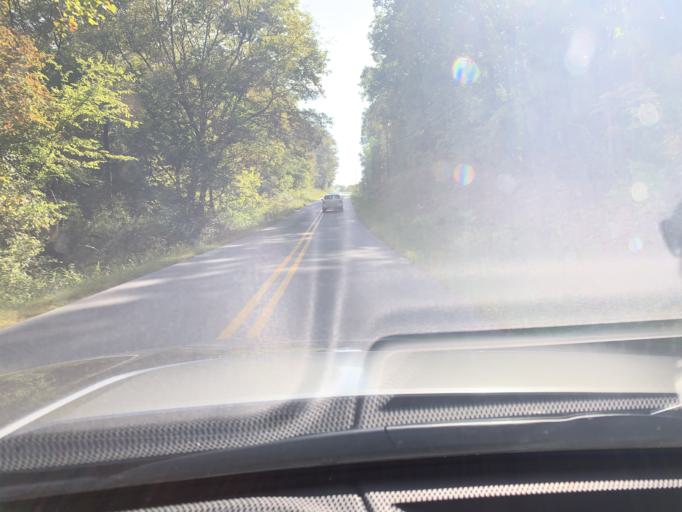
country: US
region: Georgia
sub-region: Polk County
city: Aragon
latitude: 34.0327
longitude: -85.0294
